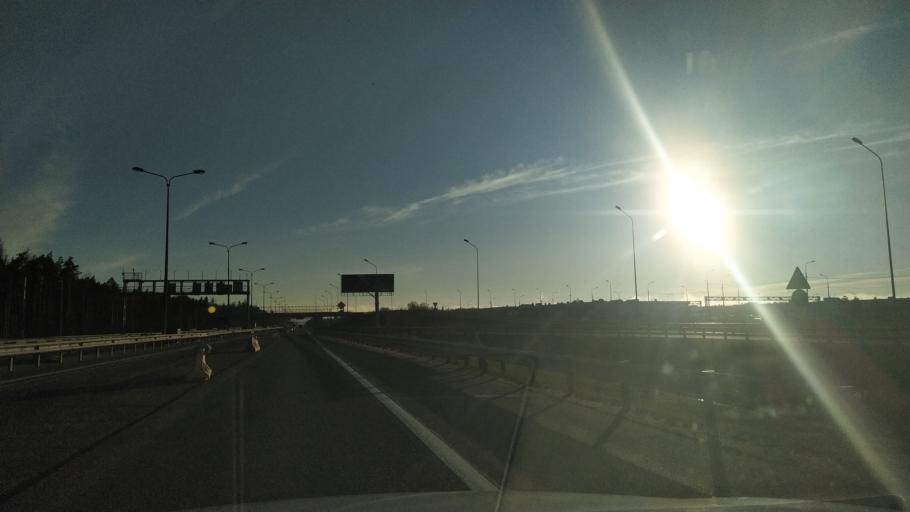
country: RU
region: St.-Petersburg
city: Ol'gino
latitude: 60.0574
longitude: 30.1330
